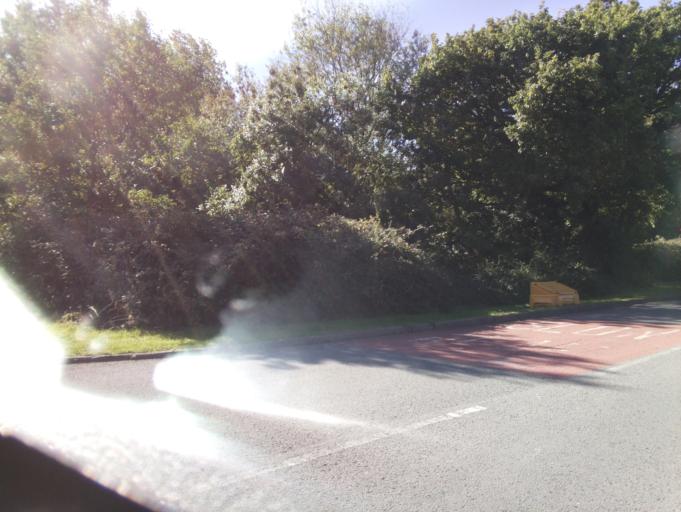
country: GB
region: Wales
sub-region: Torfaen County Borough
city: Cwmbran
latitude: 51.6503
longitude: -3.0519
